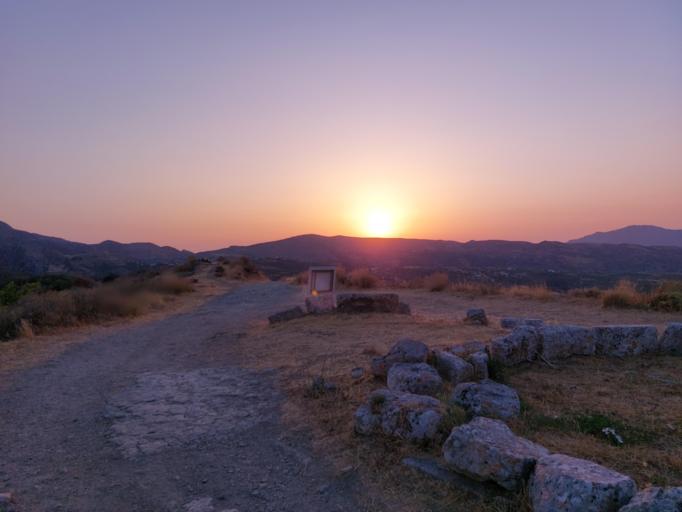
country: GR
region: Crete
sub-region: Nomos Chanias
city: Kissamos
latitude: 35.4565
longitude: 23.6527
